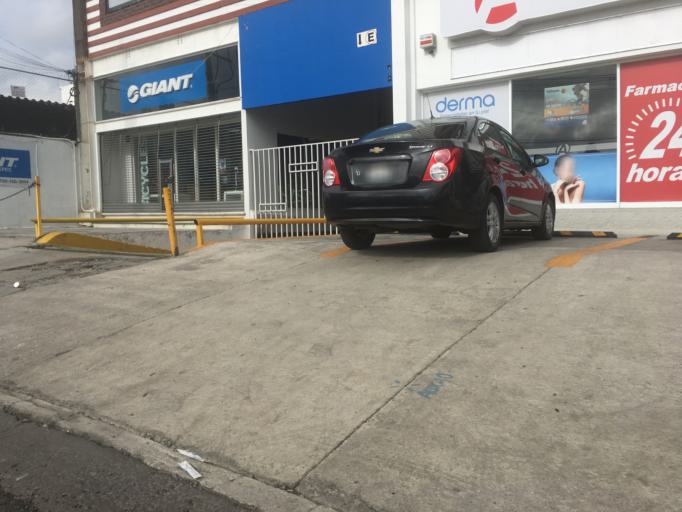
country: MX
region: Morelos
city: Metepec
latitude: 19.2755
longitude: -99.6070
